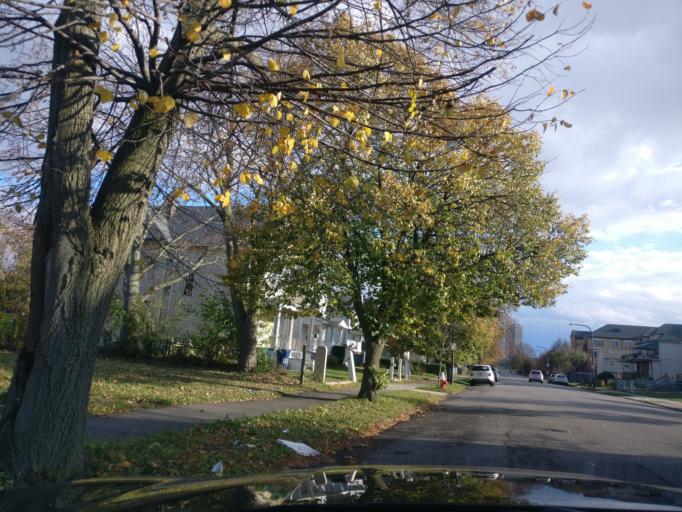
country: US
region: New York
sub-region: Erie County
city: Buffalo
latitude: 42.8965
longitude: -78.8909
